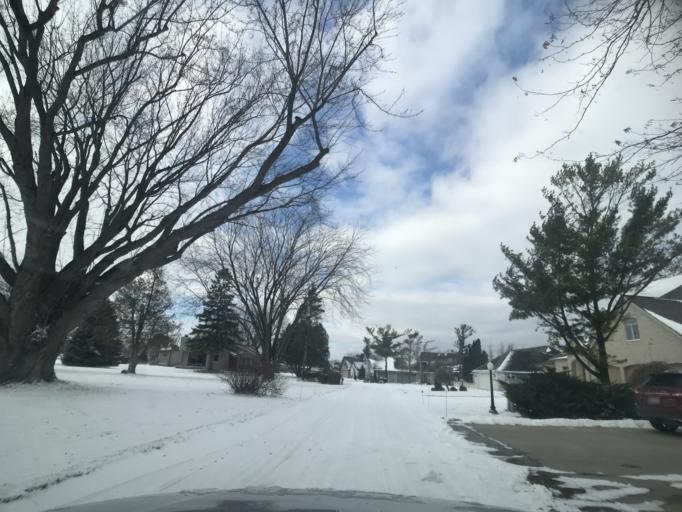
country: US
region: Wisconsin
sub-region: Door County
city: Sturgeon Bay
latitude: 44.8221
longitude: -87.3682
